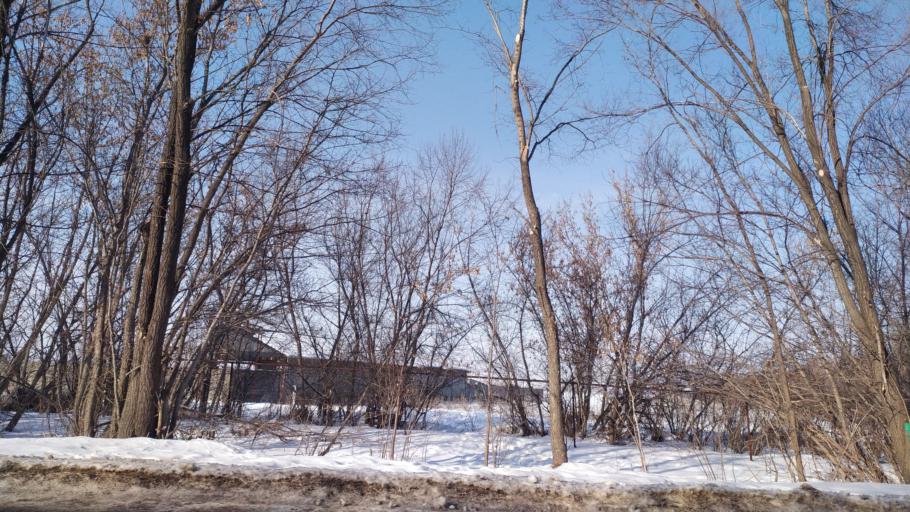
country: KZ
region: Almaty Oblysy
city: Burunday
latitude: 43.2407
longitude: 76.4244
